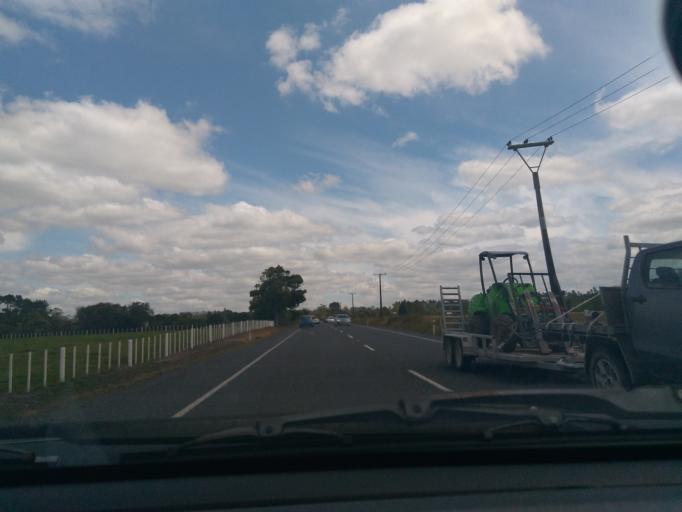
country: NZ
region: Northland
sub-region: Far North District
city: Kerikeri
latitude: -35.2264
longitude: 173.9205
